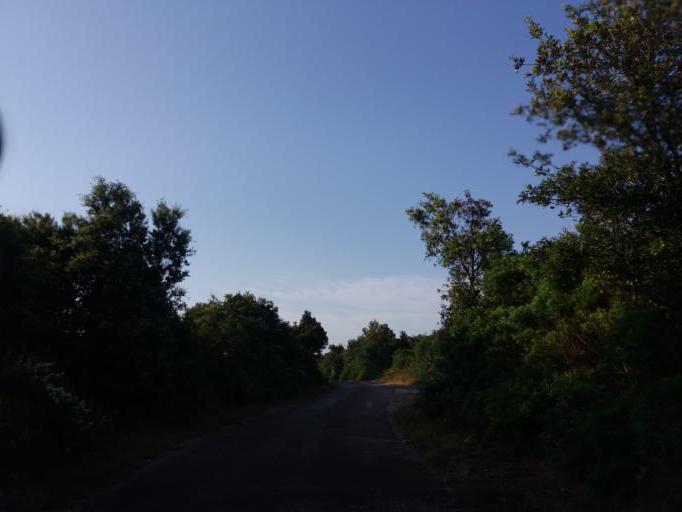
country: HR
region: Zadarska
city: Sali
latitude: 43.9095
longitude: 15.1382
